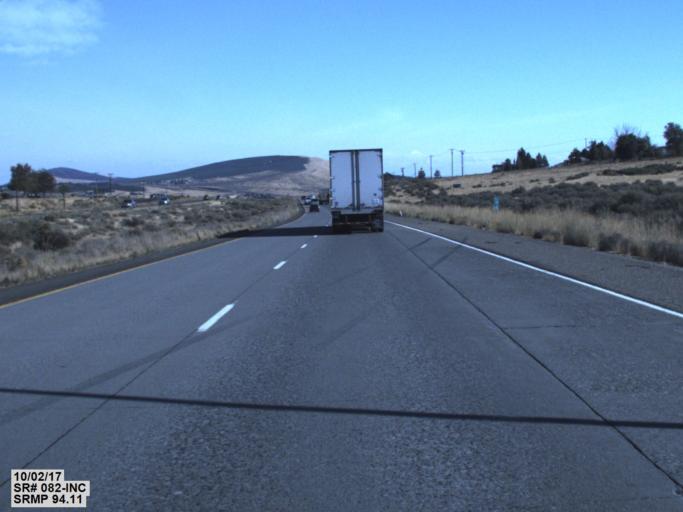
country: US
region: Washington
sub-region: Benton County
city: Benton City
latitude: 46.2616
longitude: -119.5249
